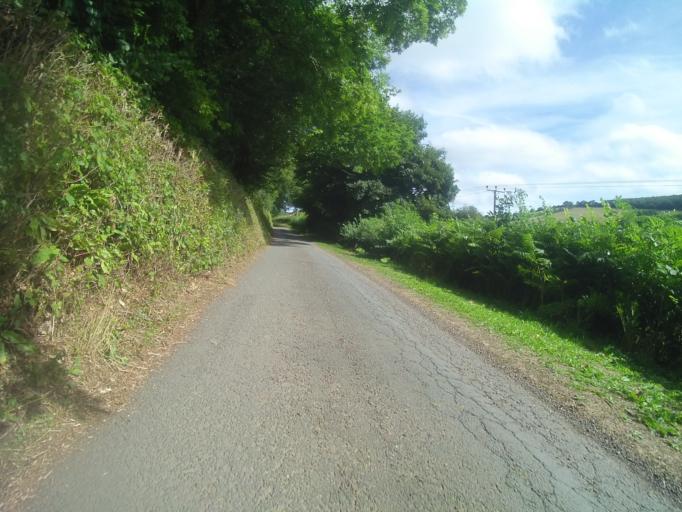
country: GB
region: England
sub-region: Devon
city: Buckfastleigh
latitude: 50.4728
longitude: -3.7599
